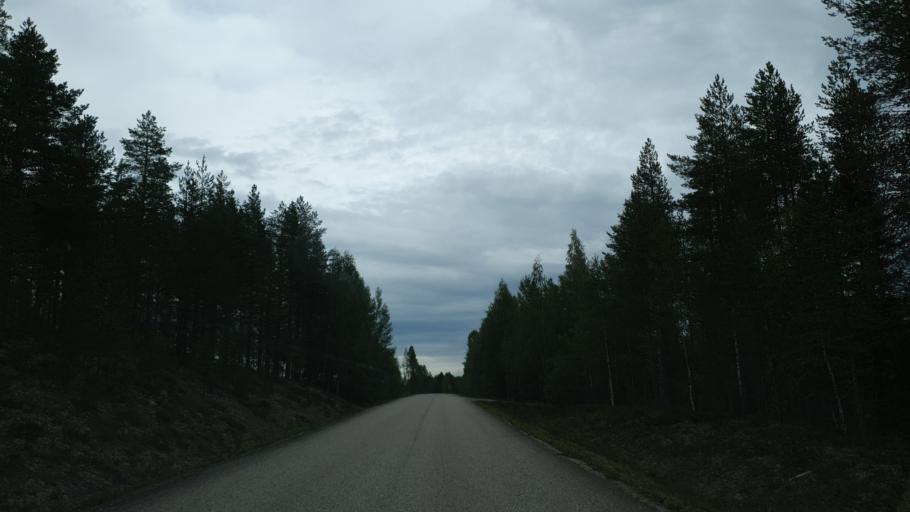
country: FI
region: Kainuu
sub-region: Kehys-Kainuu
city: Kuhmo
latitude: 64.3521
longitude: 29.0982
